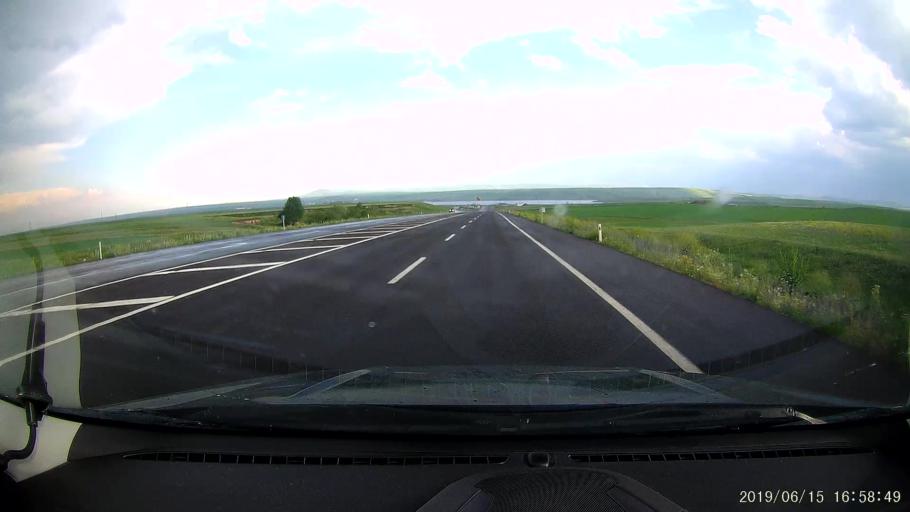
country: TR
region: Kars
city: Susuz
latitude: 40.7598
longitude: 43.1463
